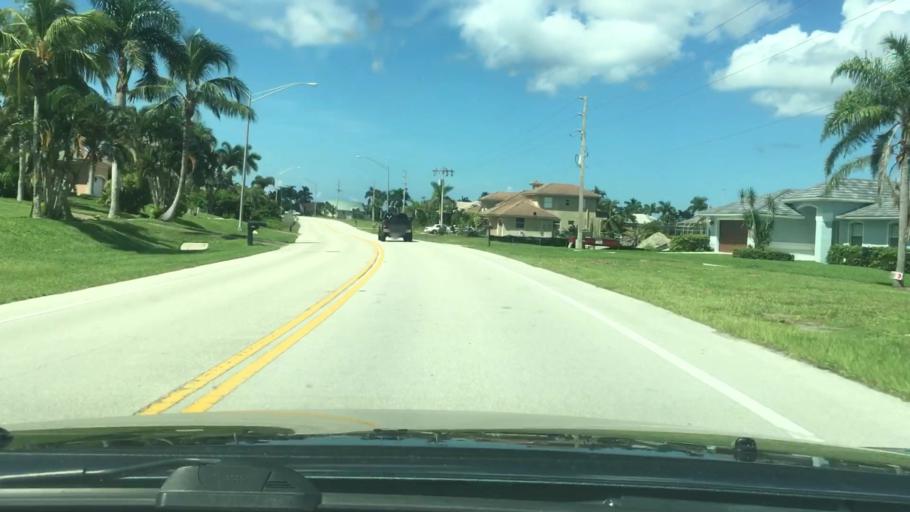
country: US
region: Florida
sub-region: Collier County
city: Marco
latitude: 25.9383
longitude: -81.6895
